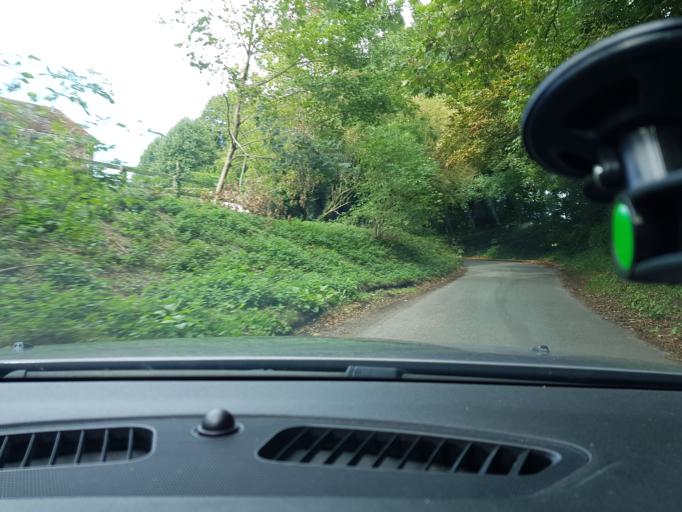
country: GB
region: England
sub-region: West Berkshire
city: Hungerford
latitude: 51.3954
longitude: -1.4859
